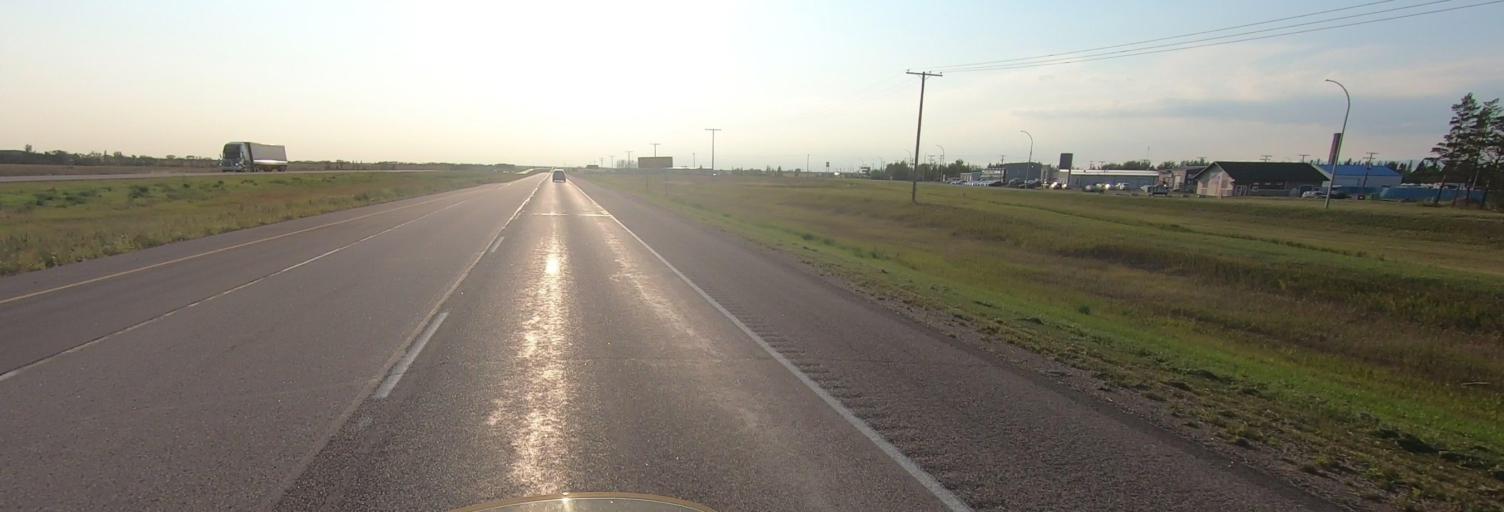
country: CA
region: Saskatchewan
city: Indian Head
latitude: 50.5256
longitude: -103.6651
